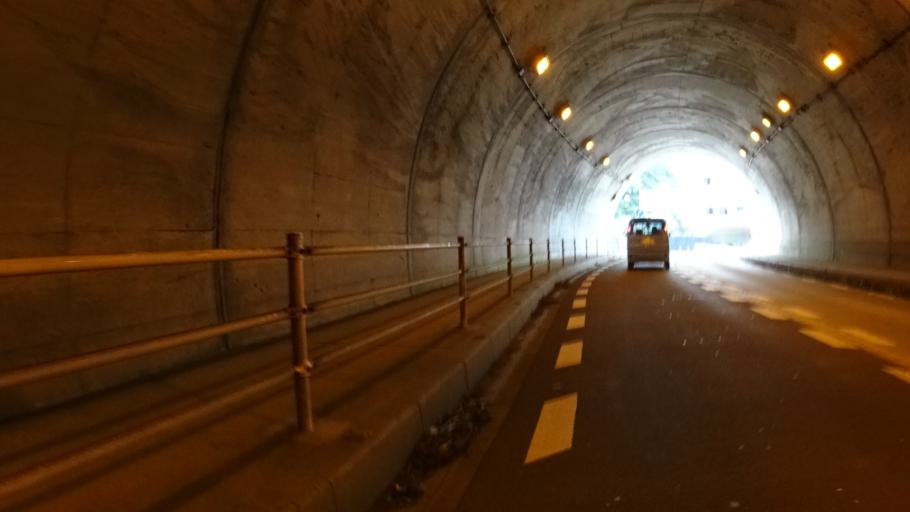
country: JP
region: Kanagawa
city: Yokosuka
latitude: 35.2308
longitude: 139.7230
